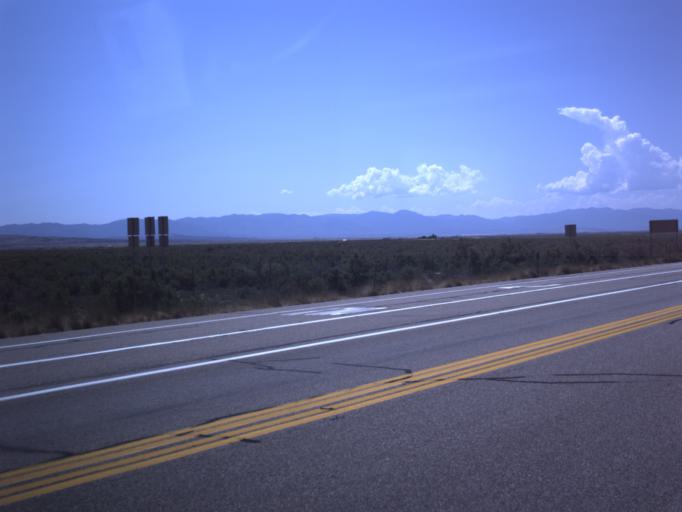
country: US
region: Utah
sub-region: Millard County
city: Delta
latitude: 39.3530
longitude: -112.4966
